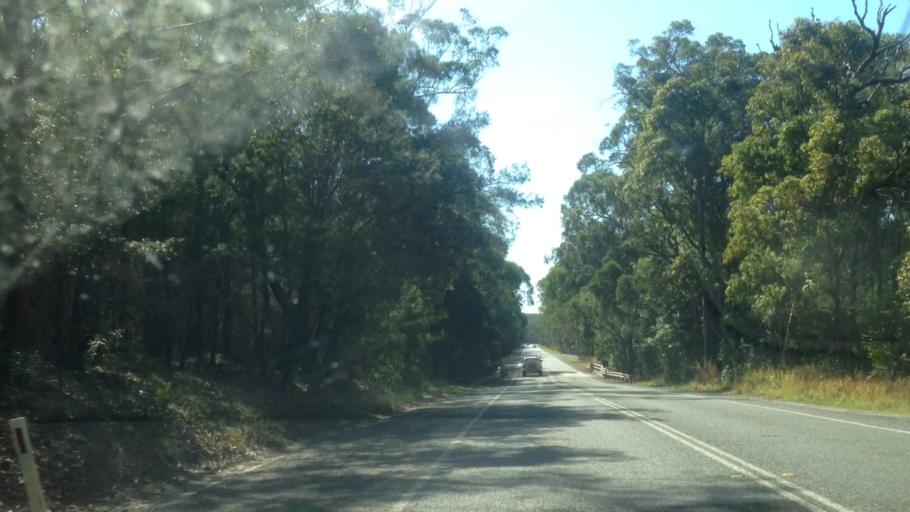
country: AU
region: New South Wales
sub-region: Lake Macquarie Shire
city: Toronto
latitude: -32.9877
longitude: 151.5063
